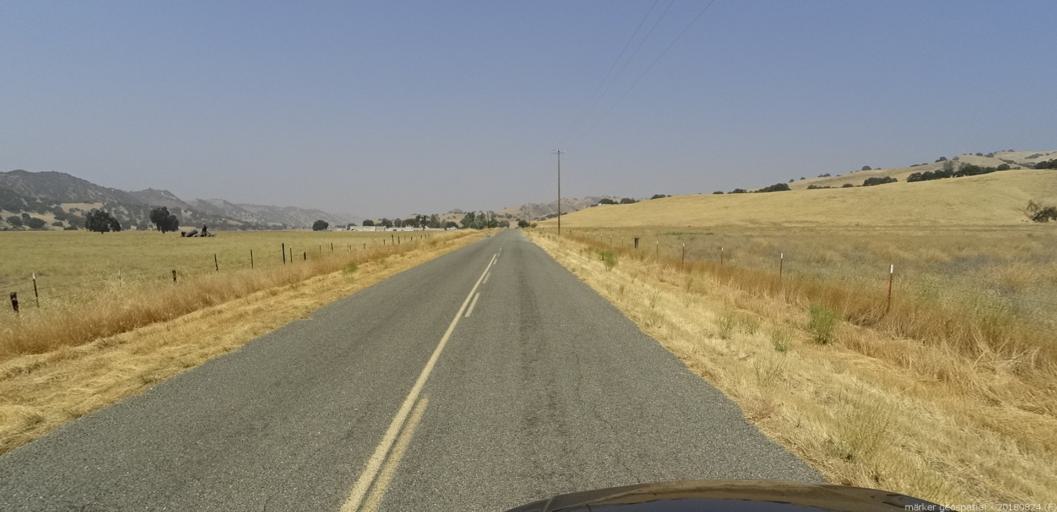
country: US
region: California
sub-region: Monterey County
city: King City
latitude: 36.1817
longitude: -120.7989
